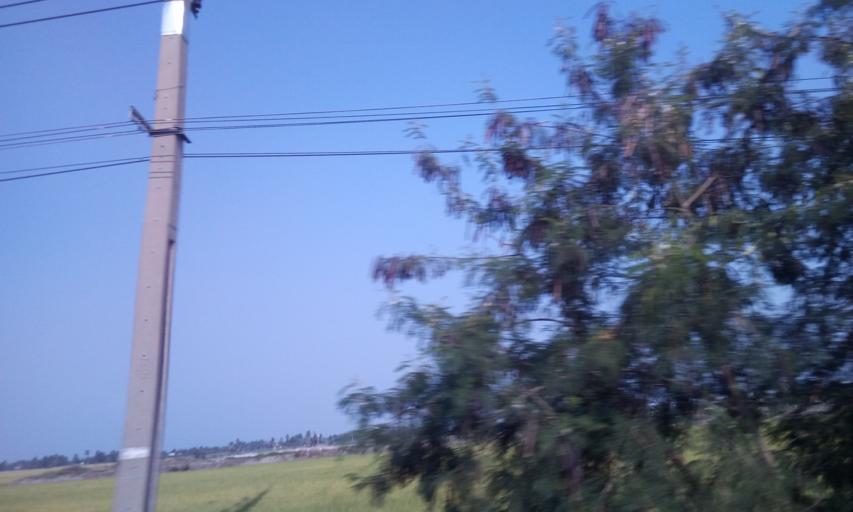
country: TH
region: Nonthaburi
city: Sai Noi
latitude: 14.0356
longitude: 100.3122
